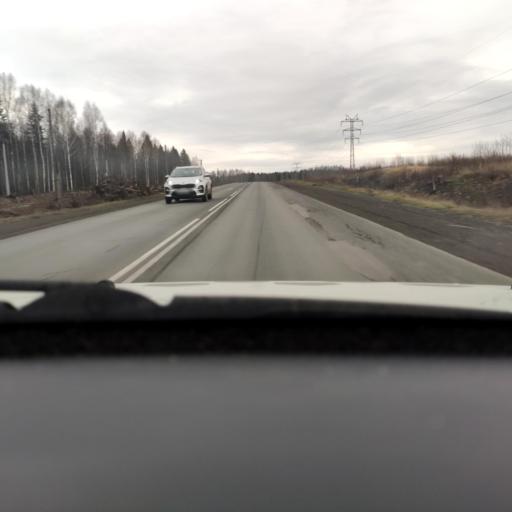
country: RU
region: Perm
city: Polazna
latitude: 58.1355
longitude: 56.4123
